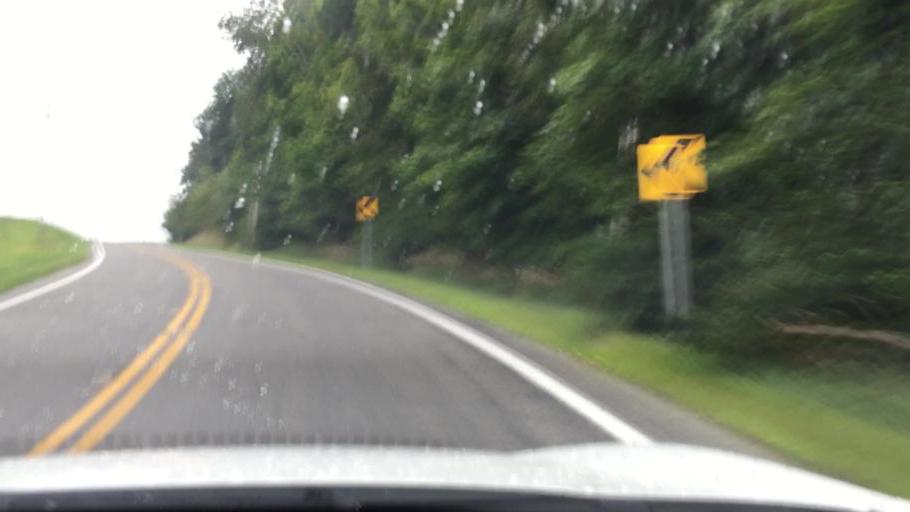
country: US
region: Ohio
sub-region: Champaign County
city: Mechanicsburg
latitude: 40.0200
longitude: -83.6374
